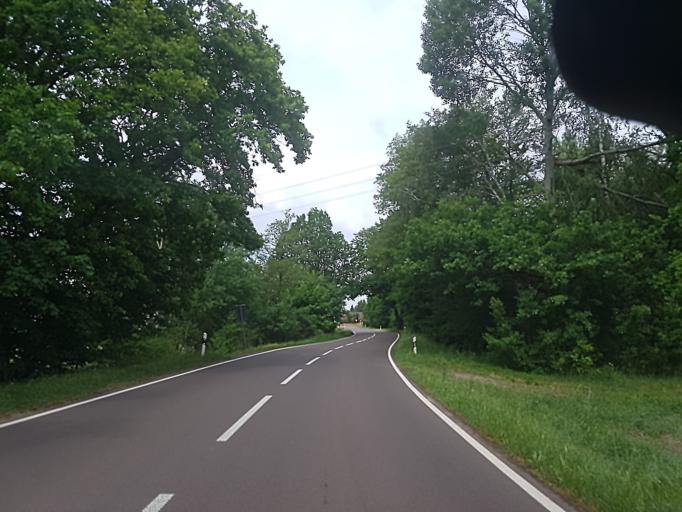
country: DE
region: Saxony-Anhalt
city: Lindau
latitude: 52.1062
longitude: 12.1952
